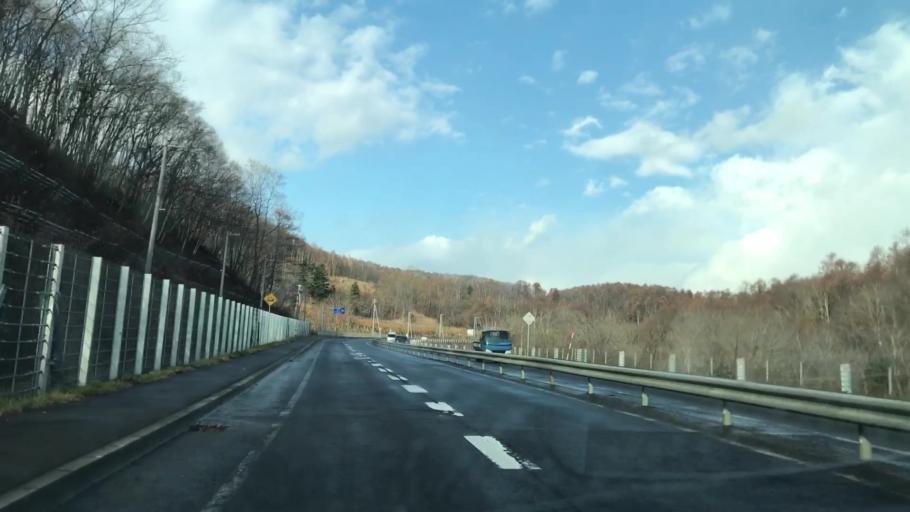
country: JP
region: Hokkaido
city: Yoichi
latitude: 43.2149
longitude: 140.7462
